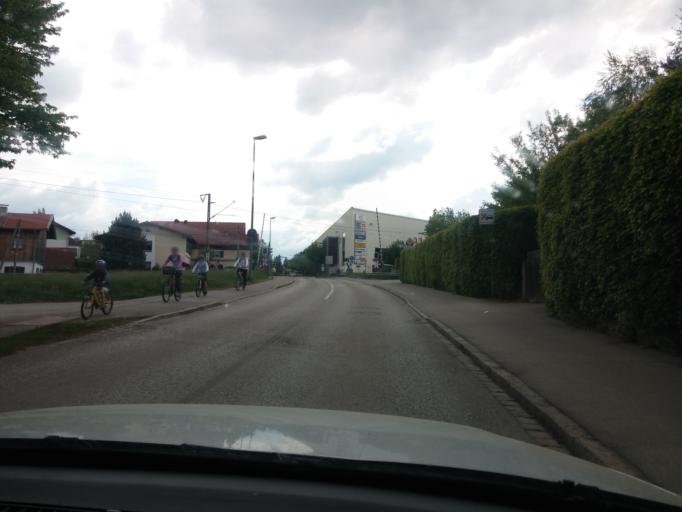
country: DE
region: Bavaria
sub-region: Upper Bavaria
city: Holzkirchen
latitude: 47.8828
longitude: 11.7046
